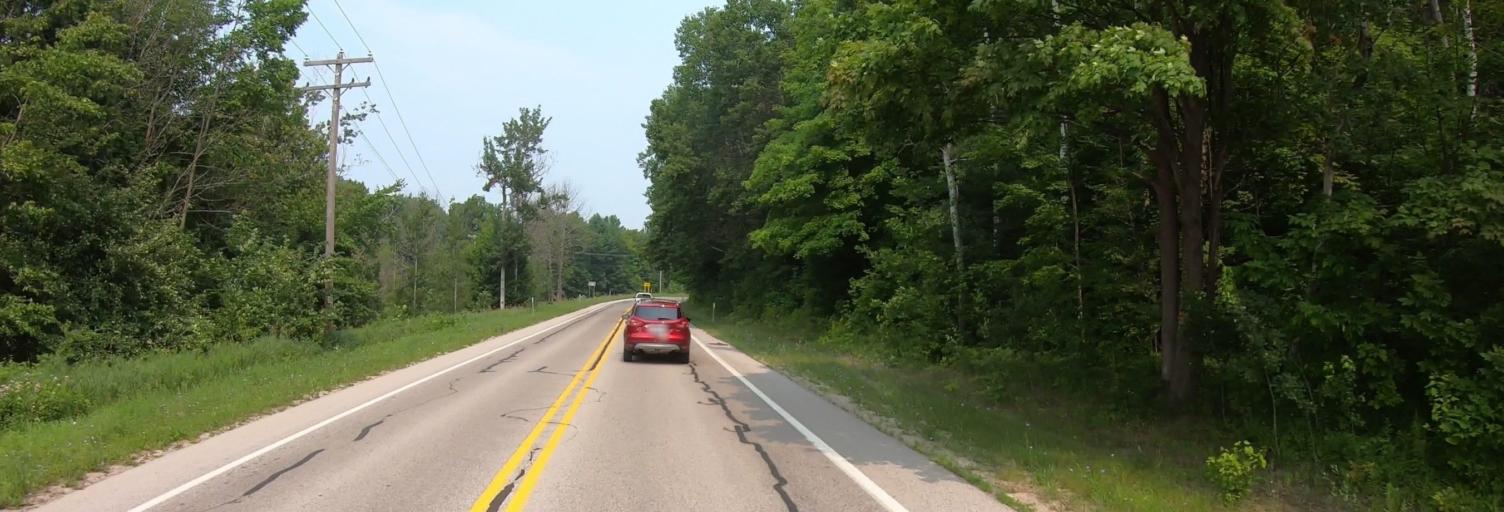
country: US
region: Michigan
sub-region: Leelanau County
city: Leland
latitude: 45.1127
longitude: -85.6313
